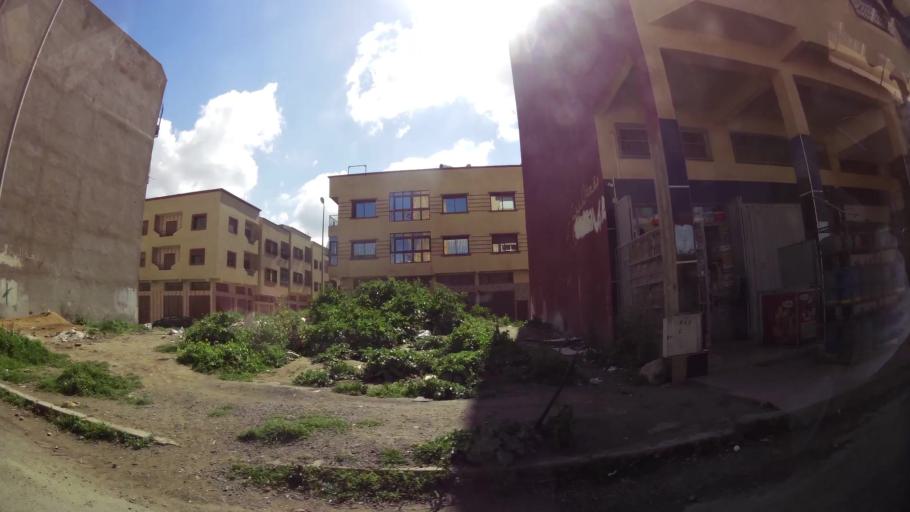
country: MA
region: Grand Casablanca
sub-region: Mediouna
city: Mediouna
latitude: 33.4564
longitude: -7.5080
